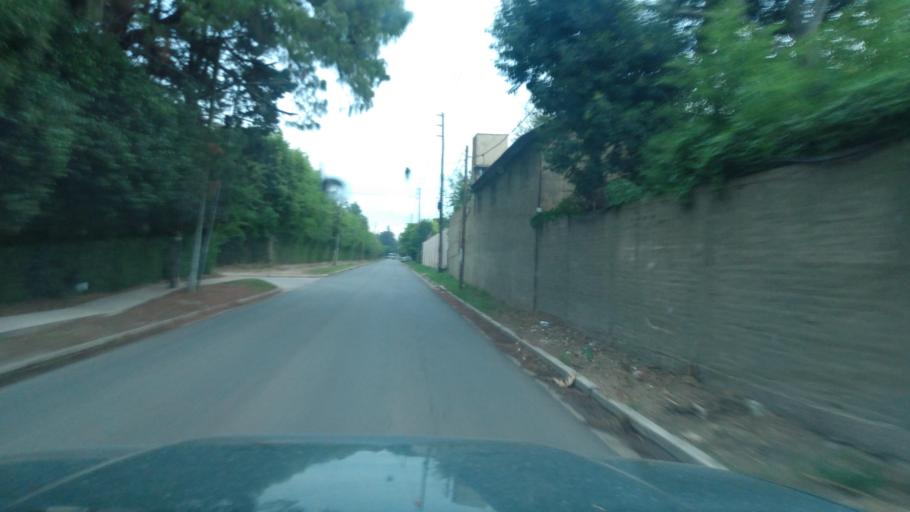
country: AR
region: Buenos Aires
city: Hurlingham
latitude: -34.5687
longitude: -58.7125
